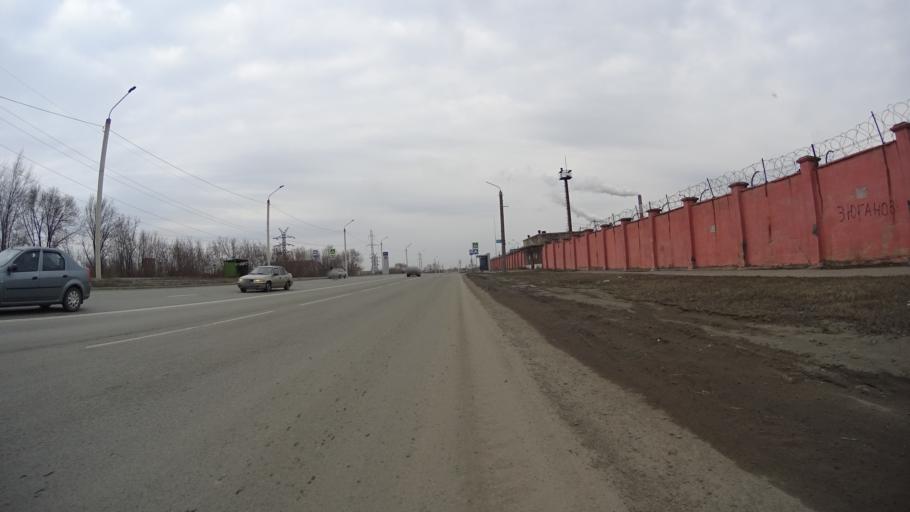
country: RU
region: Chelyabinsk
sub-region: Gorod Chelyabinsk
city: Chelyabinsk
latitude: 55.1581
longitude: 61.4838
